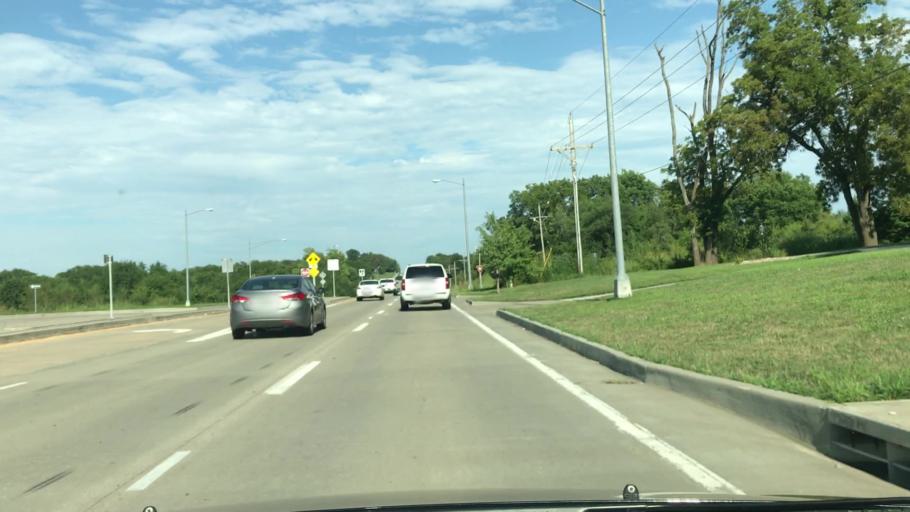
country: US
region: Missouri
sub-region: Cass County
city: Raymore
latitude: 38.8547
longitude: -94.4502
